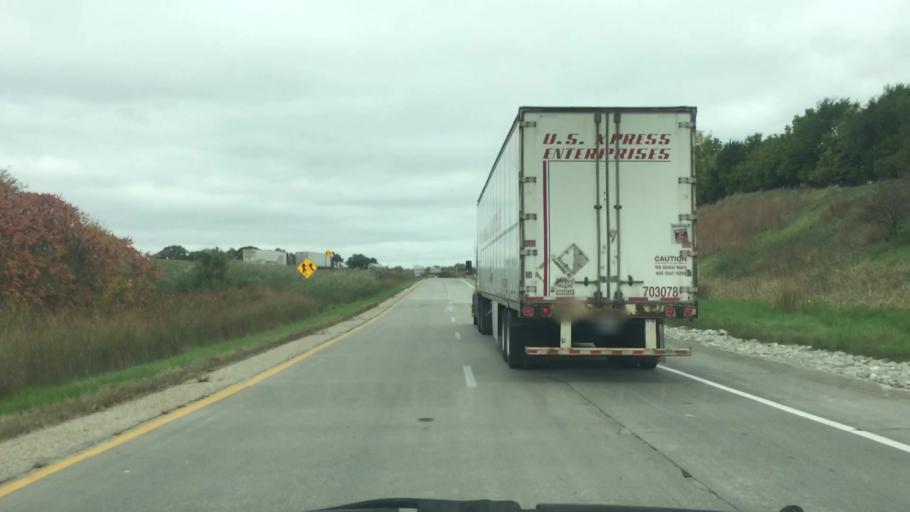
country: US
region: Iowa
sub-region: Polk County
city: Clive
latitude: 41.6156
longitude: -93.7759
